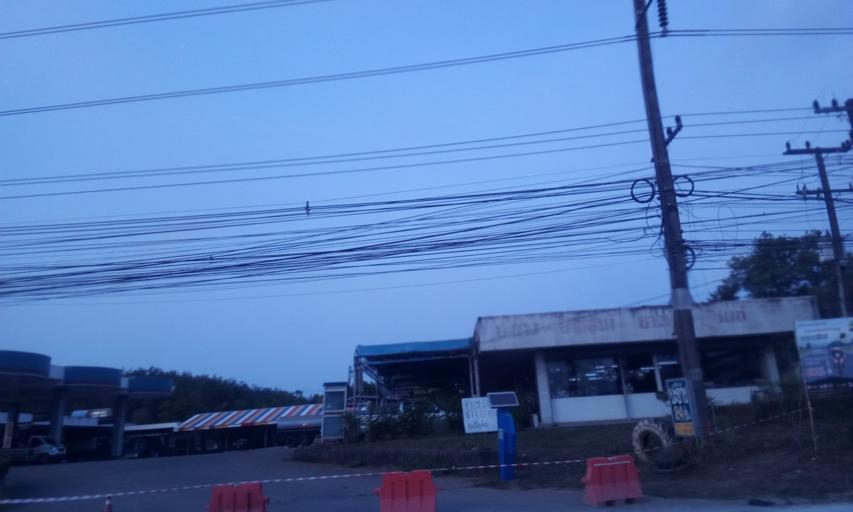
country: TH
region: Trat
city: Khao Saming
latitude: 12.3714
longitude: 102.3884
